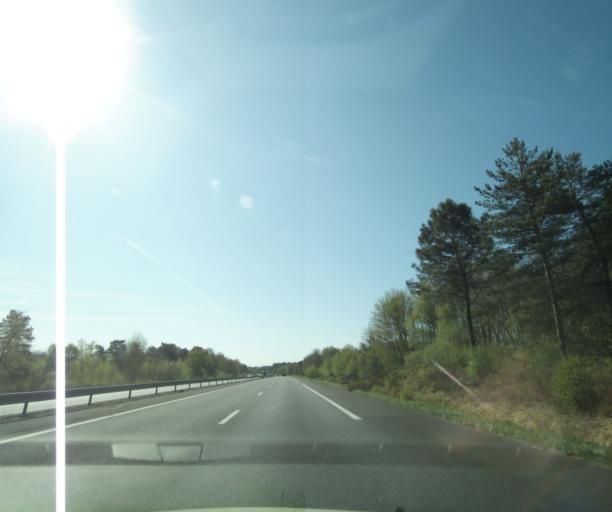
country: FR
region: Centre
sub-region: Departement du Loir-et-Cher
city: Chaumont-sur-Tharonne
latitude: 47.6182
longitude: 1.9627
